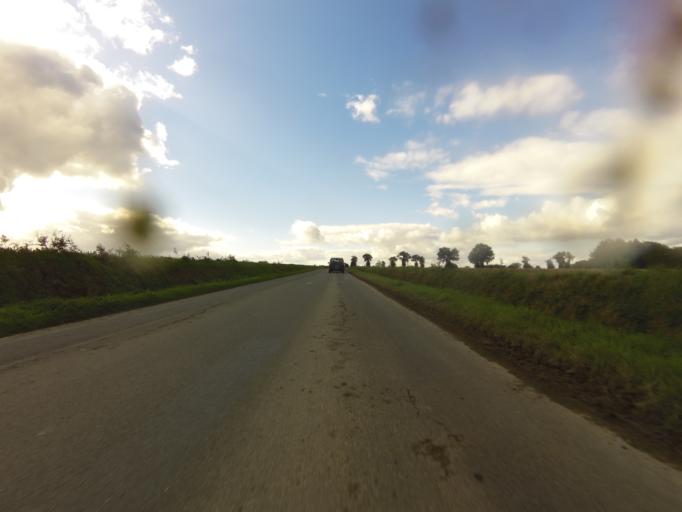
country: FR
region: Brittany
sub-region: Departement d'Ille-et-Vilaine
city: Erce-pres-Liffre
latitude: 48.2553
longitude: -1.5224
